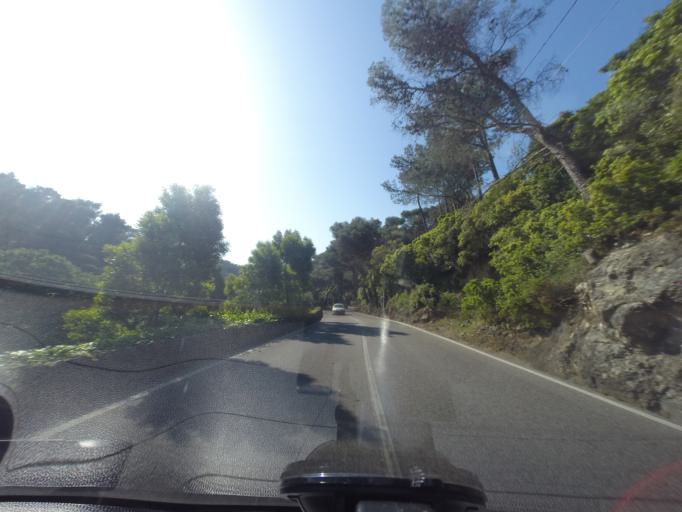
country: PT
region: Lisbon
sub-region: Cascais
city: Alcabideche
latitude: 38.7396
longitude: -9.4245
